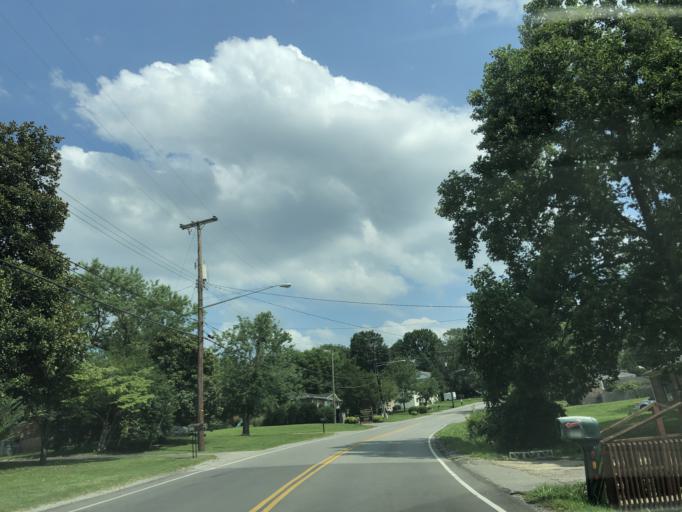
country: US
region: Tennessee
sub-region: Davidson County
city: Oak Hill
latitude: 36.0714
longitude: -86.7311
